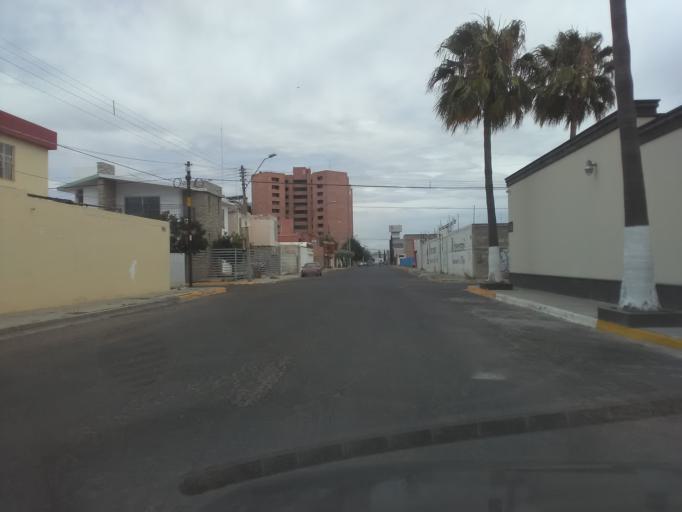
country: MX
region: Durango
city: Victoria de Durango
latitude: 24.0292
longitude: -104.6498
